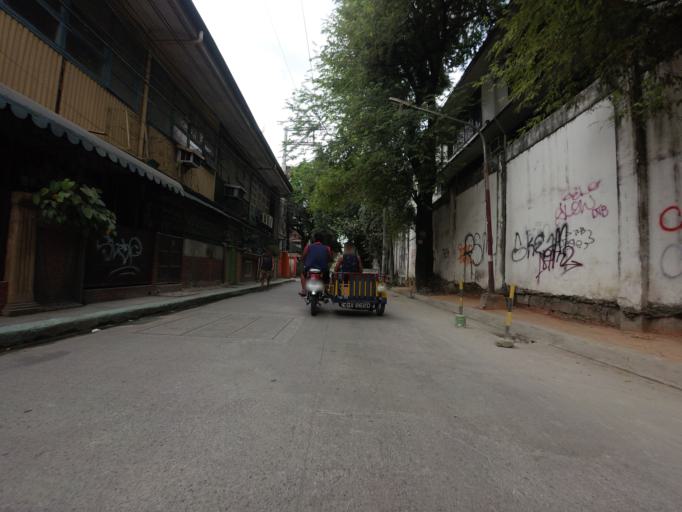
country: PH
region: Metro Manila
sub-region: Mandaluyong
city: Mandaluyong City
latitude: 14.5795
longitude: 121.0110
